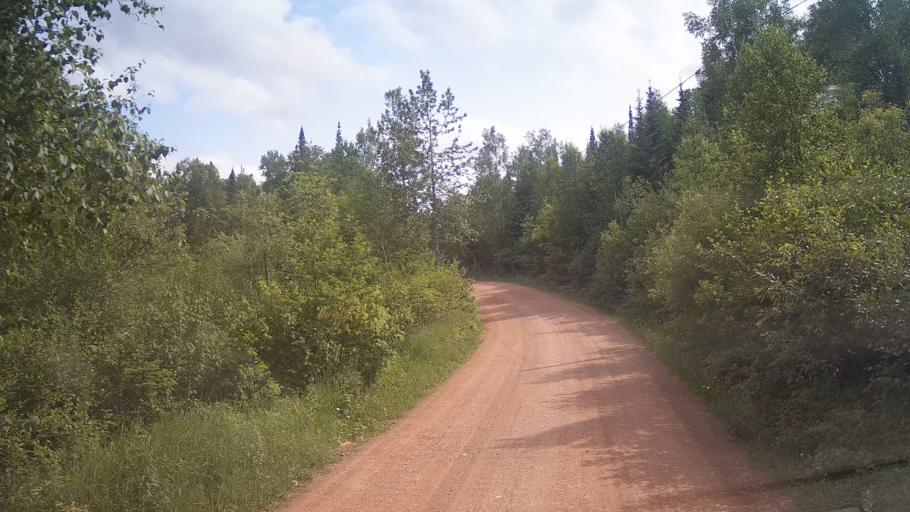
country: CA
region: Ontario
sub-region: Thunder Bay District
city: Thunder Bay
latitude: 48.6689
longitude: -88.6651
